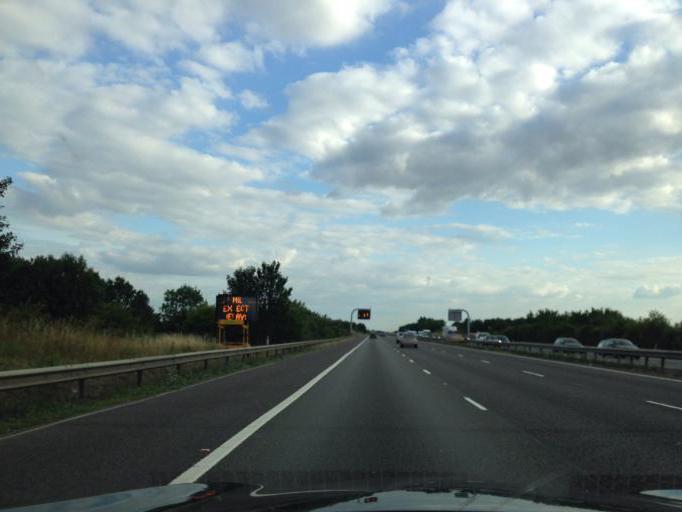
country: GB
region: England
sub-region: Oxfordshire
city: Bicester
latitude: 51.9047
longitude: -1.2056
